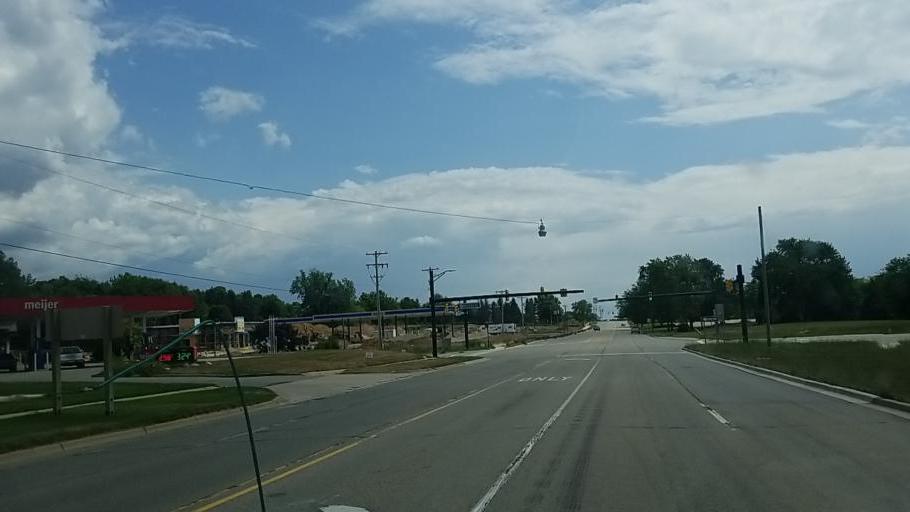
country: US
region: Michigan
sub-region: Kent County
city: Walker
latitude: 43.0194
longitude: -85.7253
